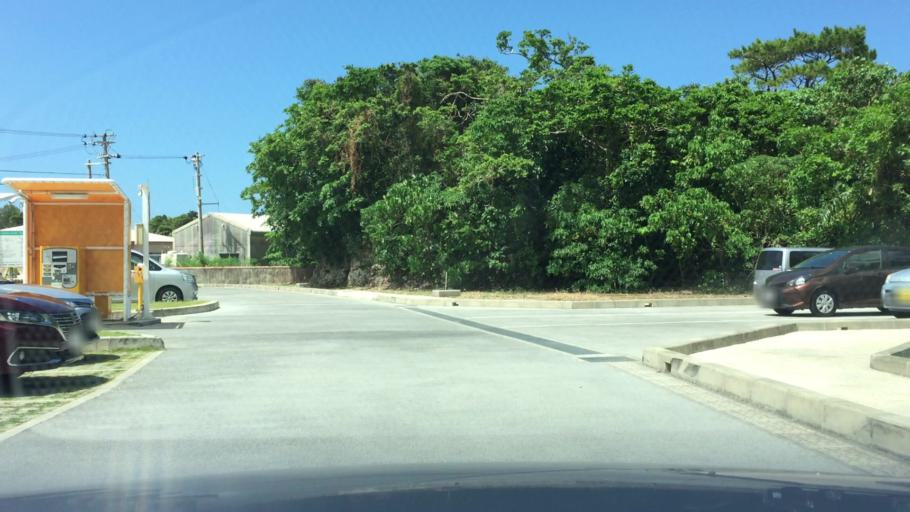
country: JP
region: Okinawa
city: Ishigaki
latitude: 24.4625
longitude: 124.1429
